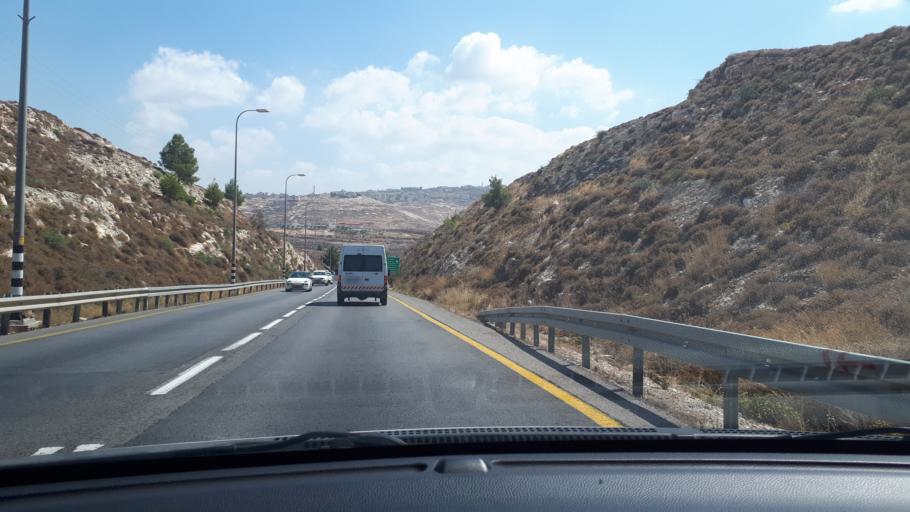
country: PS
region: West Bank
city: Mikhmas
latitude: 31.8762
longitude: 35.2654
